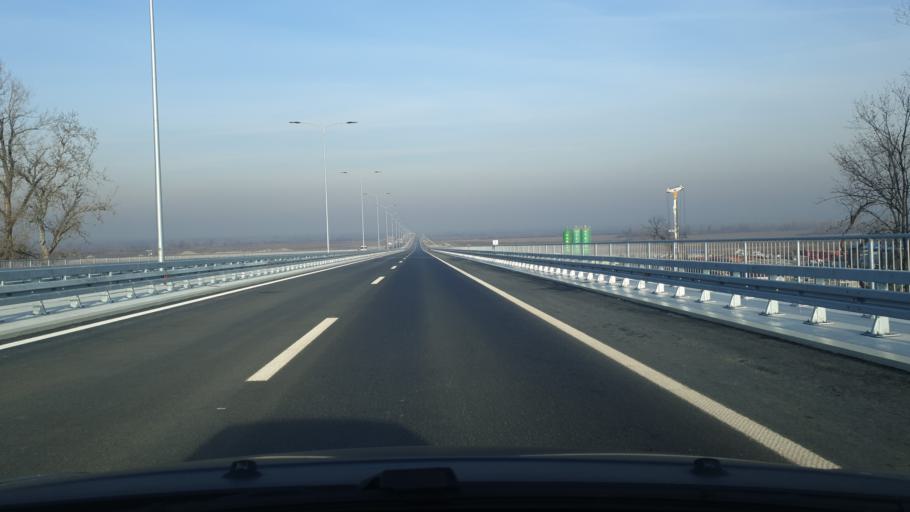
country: RS
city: Baric
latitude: 44.6687
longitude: 20.2491
